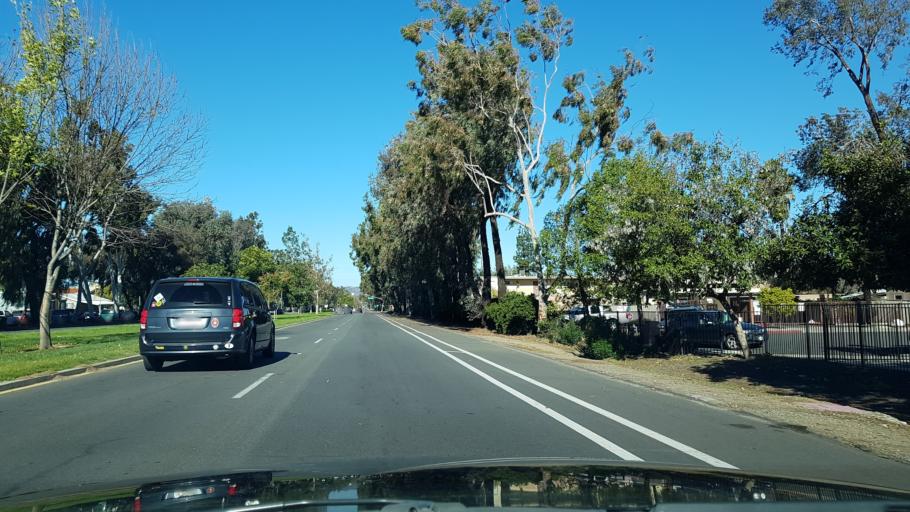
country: US
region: California
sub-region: San Diego County
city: Escondido
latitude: 33.1060
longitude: -117.0774
